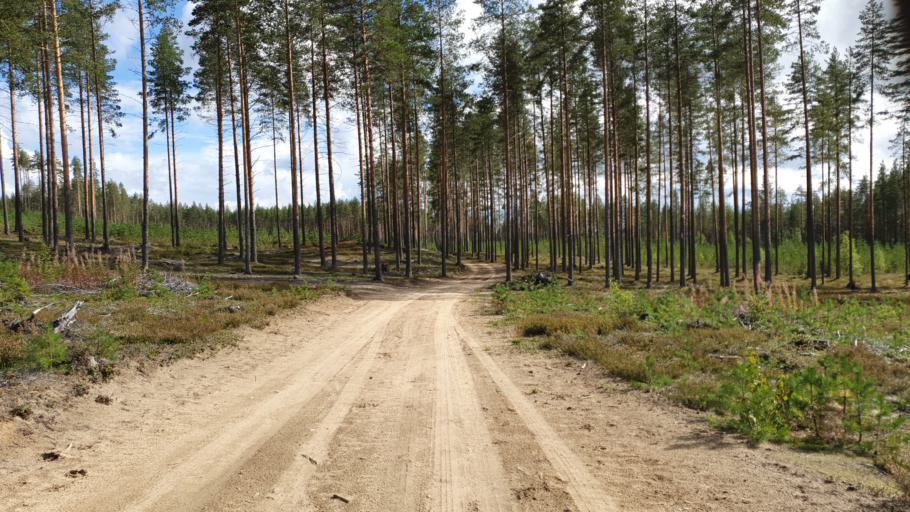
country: FI
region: Kainuu
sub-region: Kehys-Kainuu
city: Kuhmo
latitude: 64.1488
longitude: 29.3733
